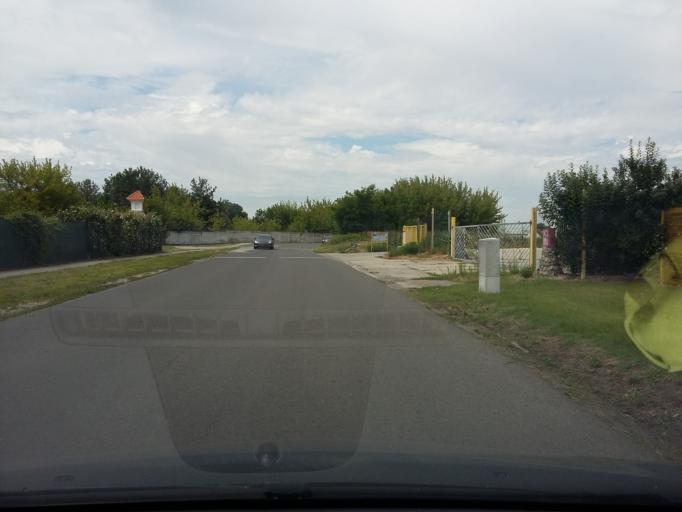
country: SK
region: Bratislavsky
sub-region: Okres Malacky
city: Malacky
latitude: 48.4301
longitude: 17.0311
